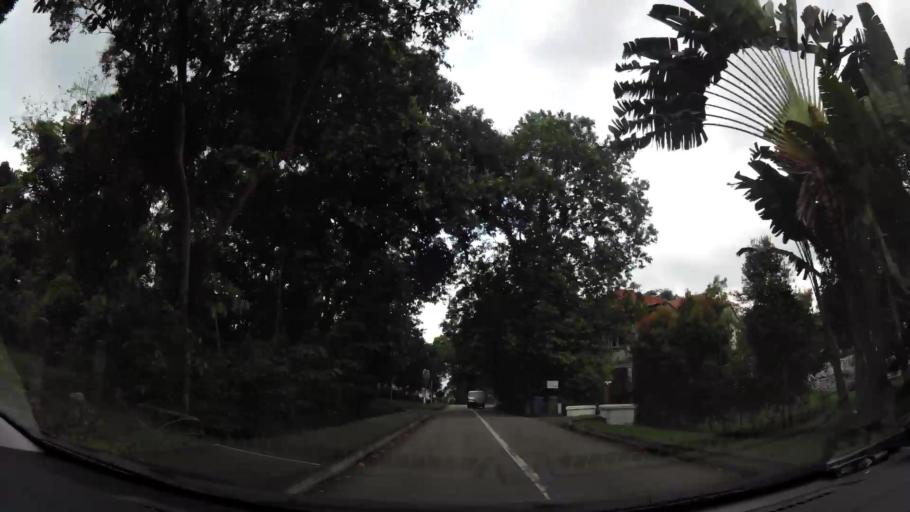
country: SG
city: Singapore
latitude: 1.2830
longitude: 103.7992
